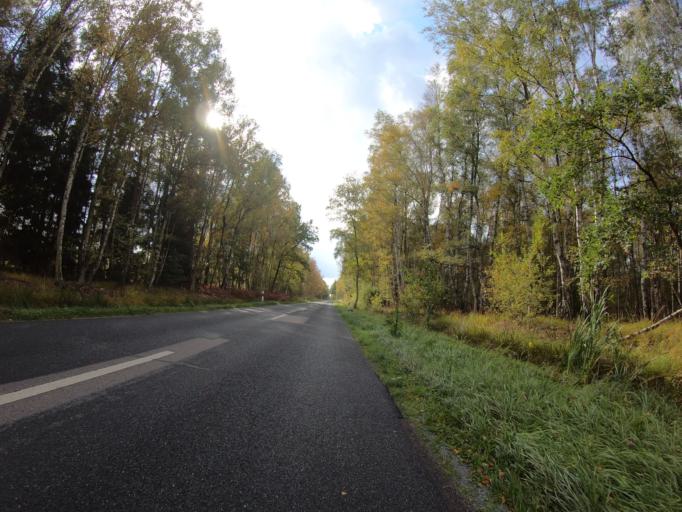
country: DE
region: Lower Saxony
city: Schoneworde
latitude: 52.5817
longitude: 10.6406
